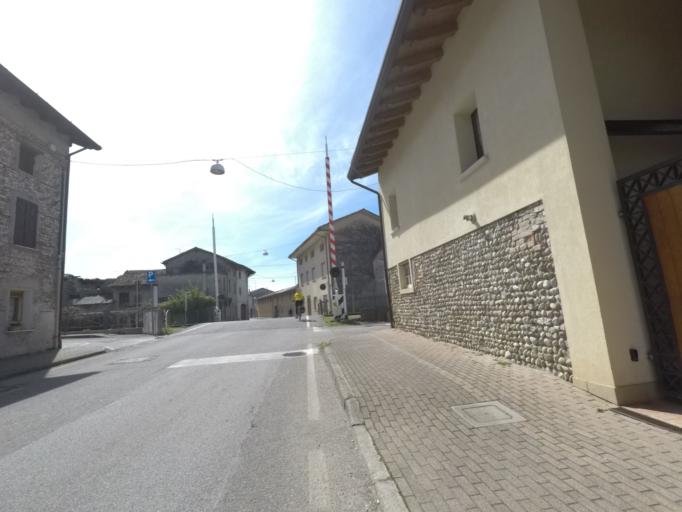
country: IT
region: Friuli Venezia Giulia
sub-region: Provincia di Pordenone
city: Casarsa della Delizia
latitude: 45.9421
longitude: 12.8363
